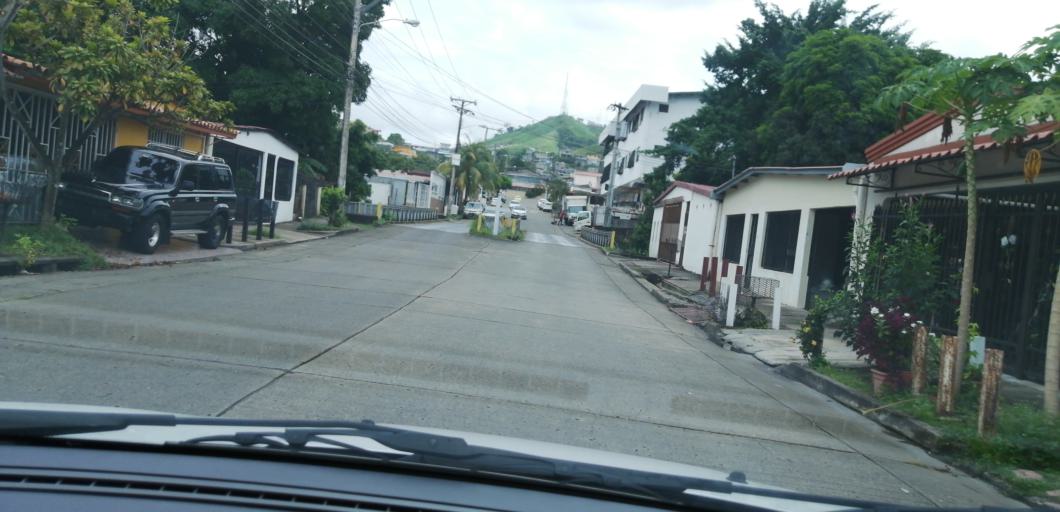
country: PA
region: Panama
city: Panama
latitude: 9.0346
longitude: -79.5178
